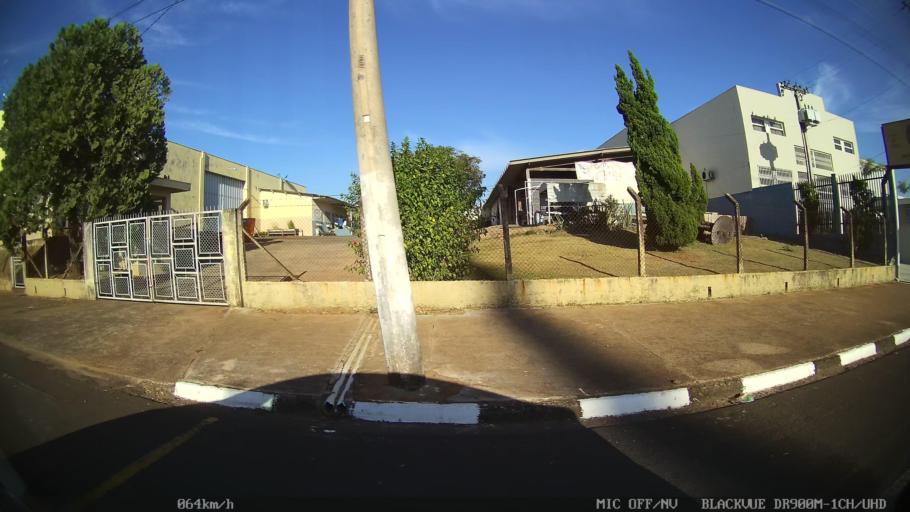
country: BR
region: Sao Paulo
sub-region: Franca
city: Franca
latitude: -20.5108
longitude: -47.3743
